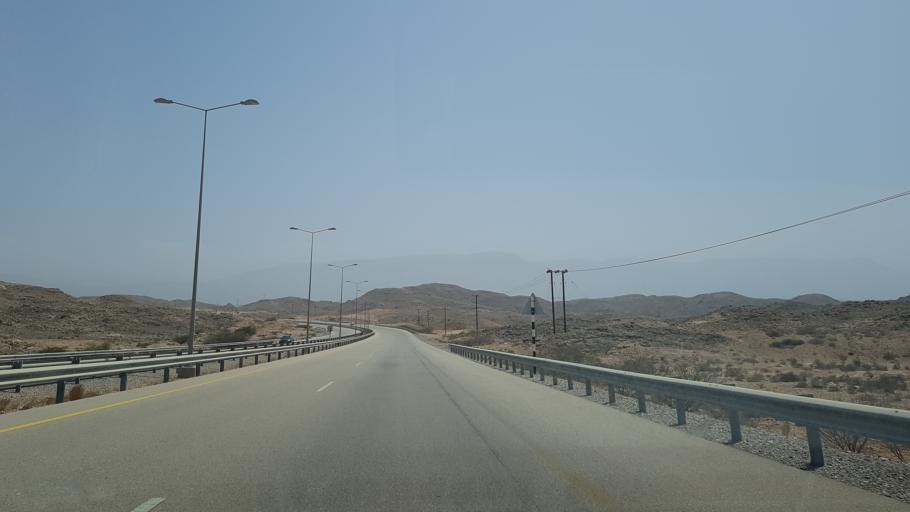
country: OM
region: Muhafazat Masqat
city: Muscat
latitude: 23.1677
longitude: 58.9761
